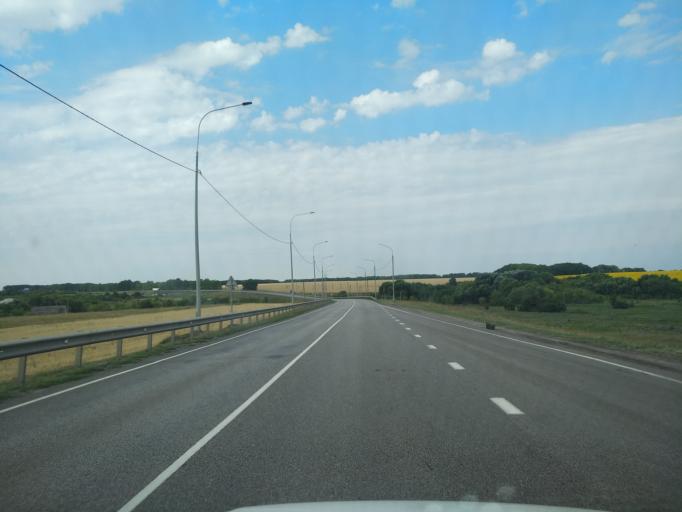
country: RU
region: Lipetsk
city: Dobrinka
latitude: 51.9150
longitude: 40.4656
